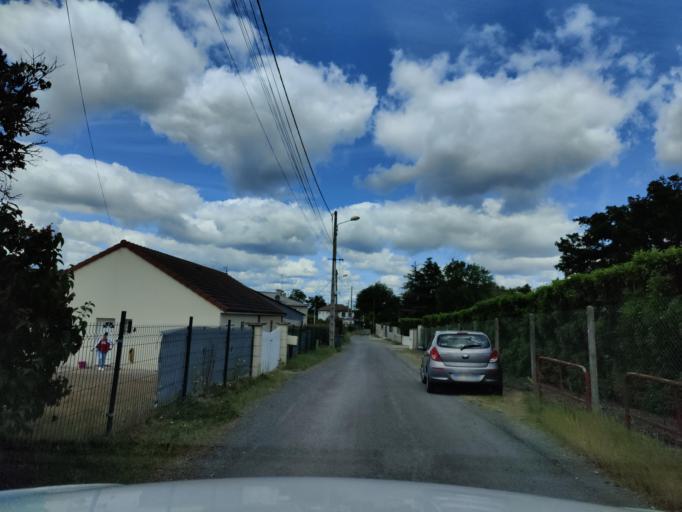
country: FR
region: Auvergne
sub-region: Departement de l'Allier
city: Saint-Victor
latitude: 46.4014
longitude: 2.6117
